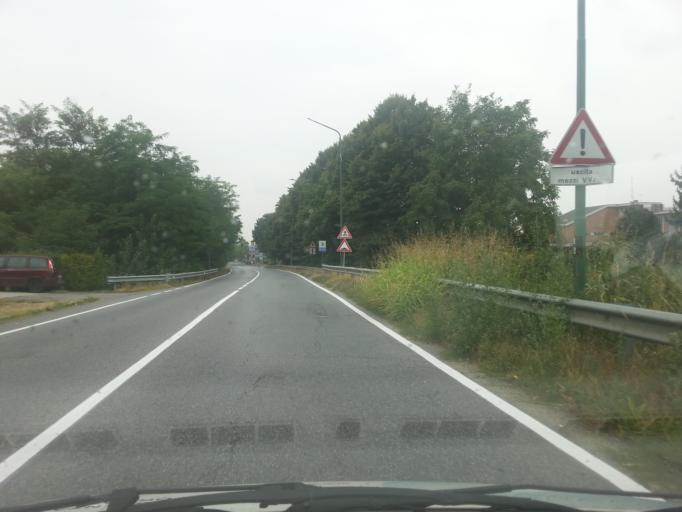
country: IT
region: Piedmont
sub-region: Provincia di Torino
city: Rivalta di Torino
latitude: 45.0359
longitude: 7.5237
